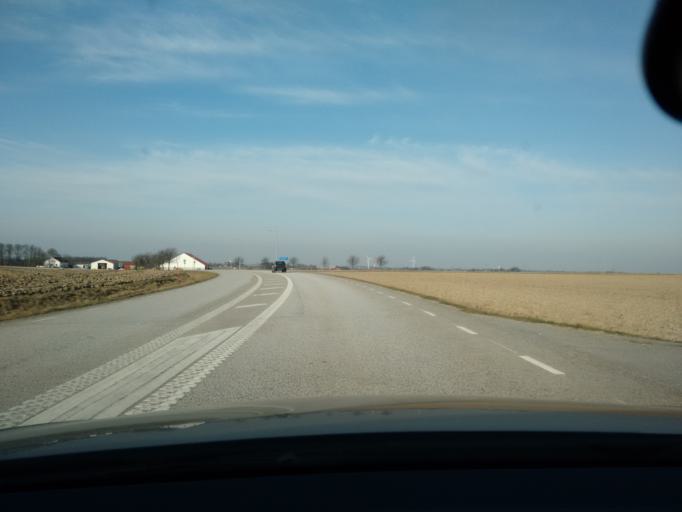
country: SE
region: Skane
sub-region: Lunds Kommun
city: Lund
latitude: 55.7452
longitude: 13.1874
